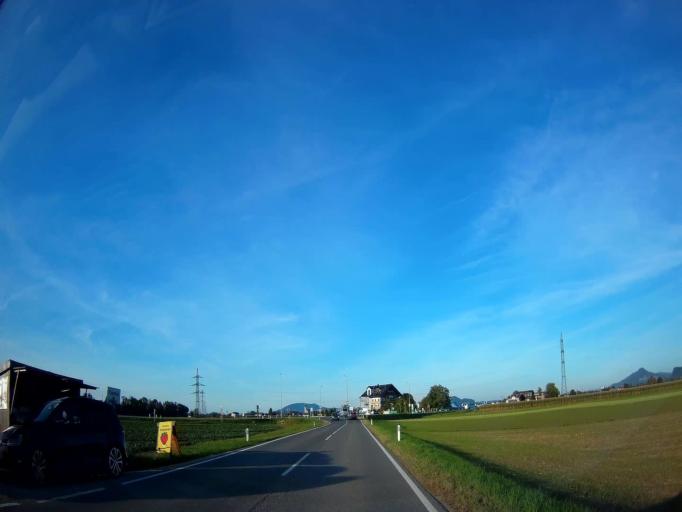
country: DE
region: Bavaria
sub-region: Upper Bavaria
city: Ainring
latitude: 47.7783
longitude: 12.9604
